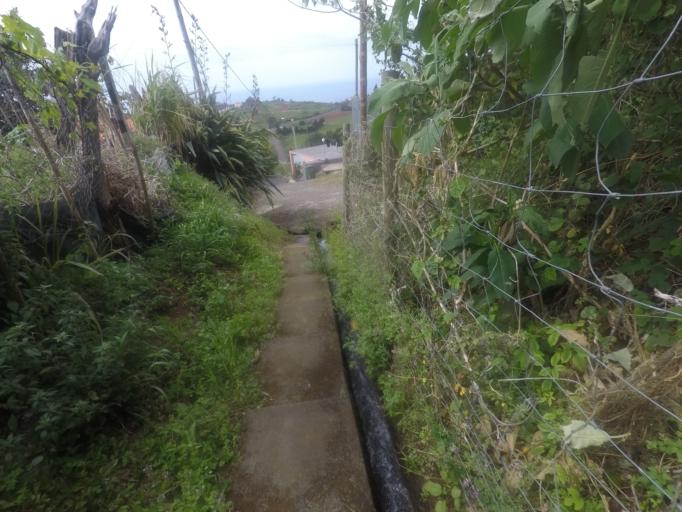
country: PT
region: Madeira
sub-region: Santana
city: Santana
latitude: 32.8213
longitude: -16.8854
